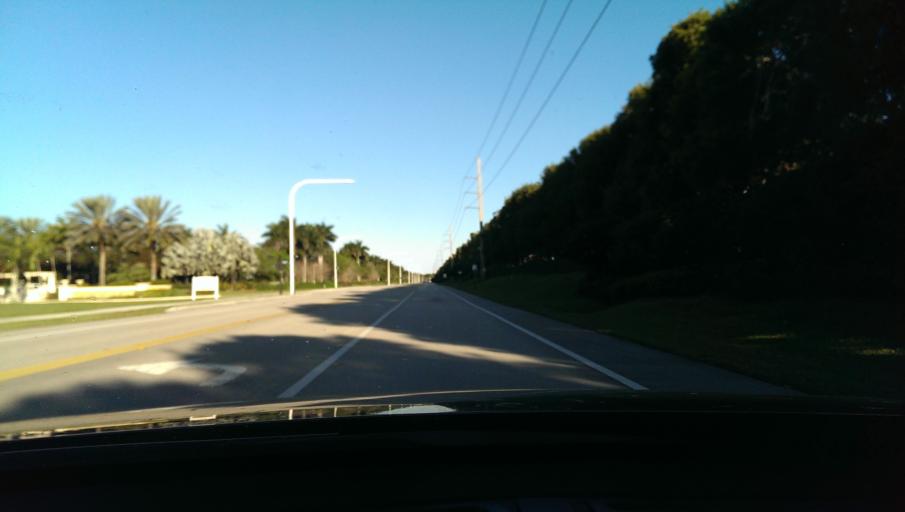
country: US
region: Florida
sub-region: Broward County
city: Weston
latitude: 26.0816
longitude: -80.4025
